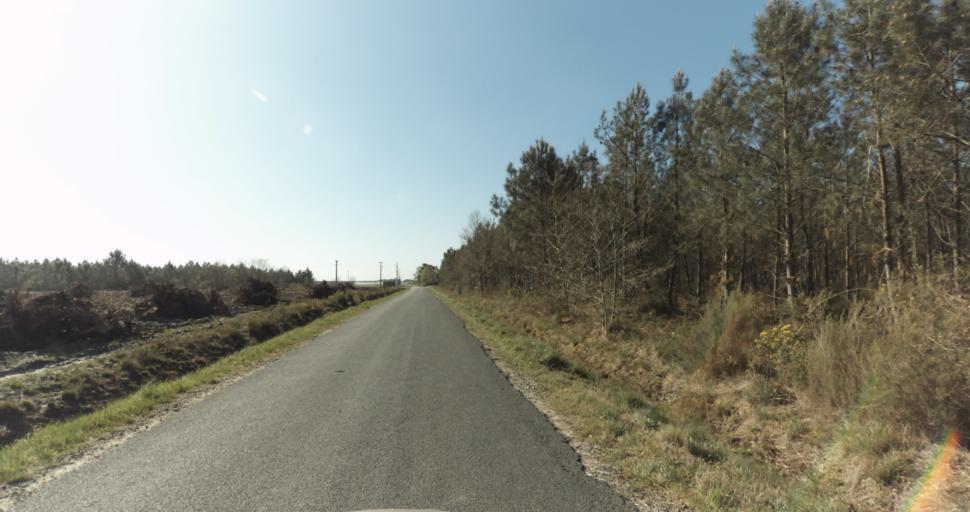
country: FR
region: Aquitaine
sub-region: Departement de la Gironde
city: Marcheprime
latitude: 44.7769
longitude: -0.8593
